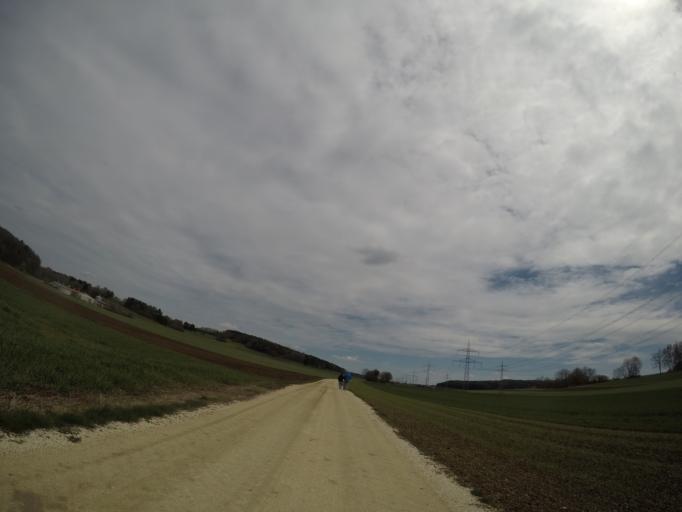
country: DE
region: Baden-Wuerttemberg
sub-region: Tuebingen Region
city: Laichingen
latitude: 48.4807
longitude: 9.6644
